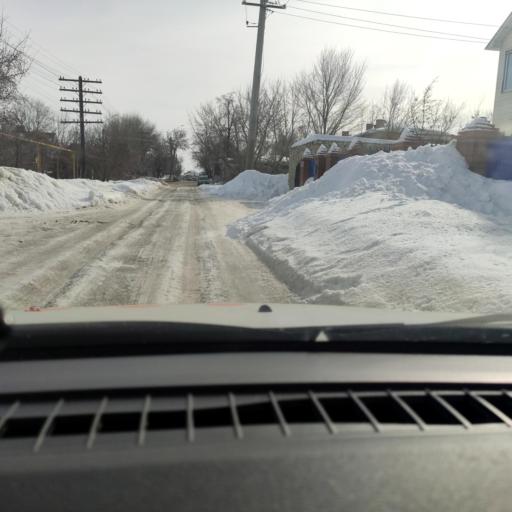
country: RU
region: Samara
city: Kinel'
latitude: 53.2331
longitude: 50.6298
